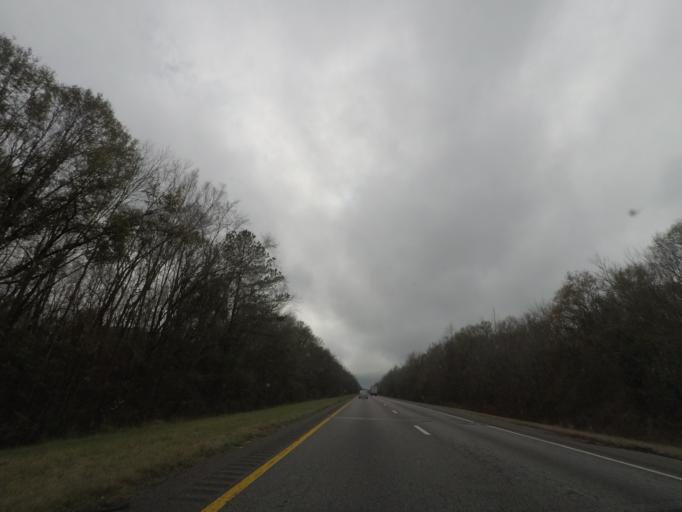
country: US
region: South Carolina
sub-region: Orangeburg County
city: Holly Hill
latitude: 33.3448
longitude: -80.5337
